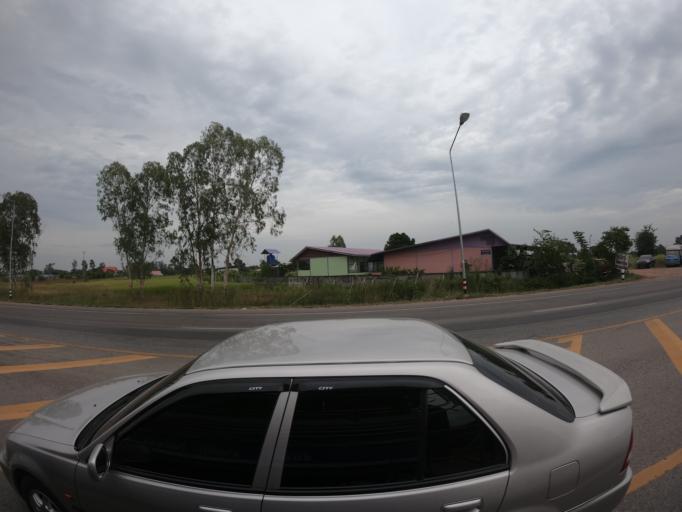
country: TH
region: Roi Et
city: Chiang Khwan
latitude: 16.1431
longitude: 103.8579
